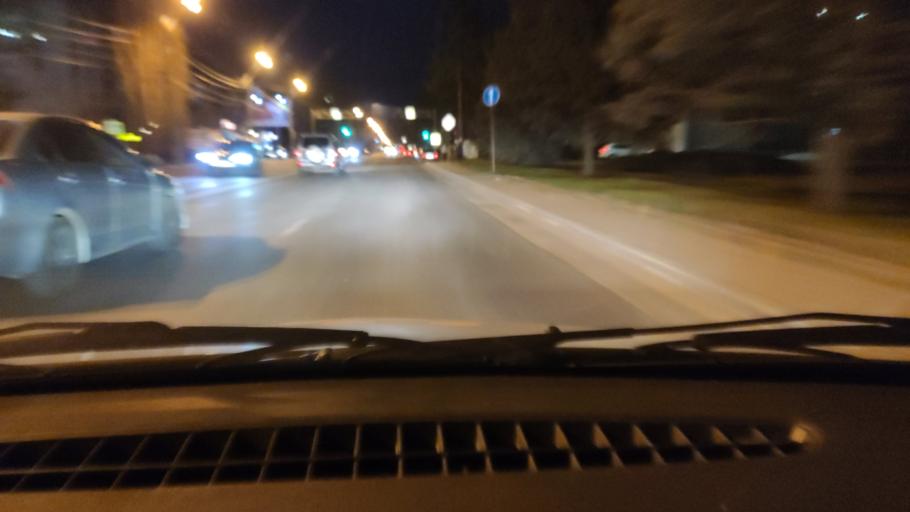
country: RU
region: Voronezj
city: Podgornoye
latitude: 51.7255
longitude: 39.1994
